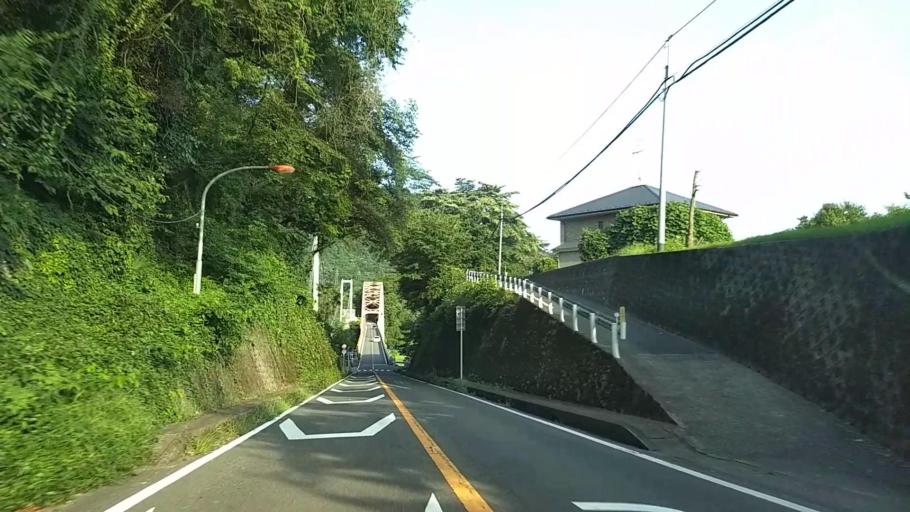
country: JP
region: Tokyo
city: Hachioji
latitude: 35.5899
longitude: 139.2654
